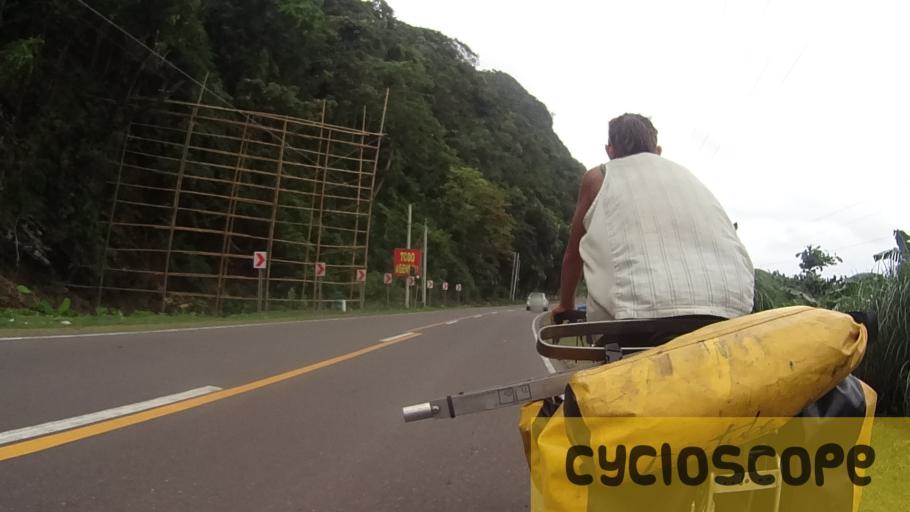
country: PH
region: Western Visayas
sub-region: Province of Aklan
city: Gibong
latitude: 11.8655
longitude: 122.0366
